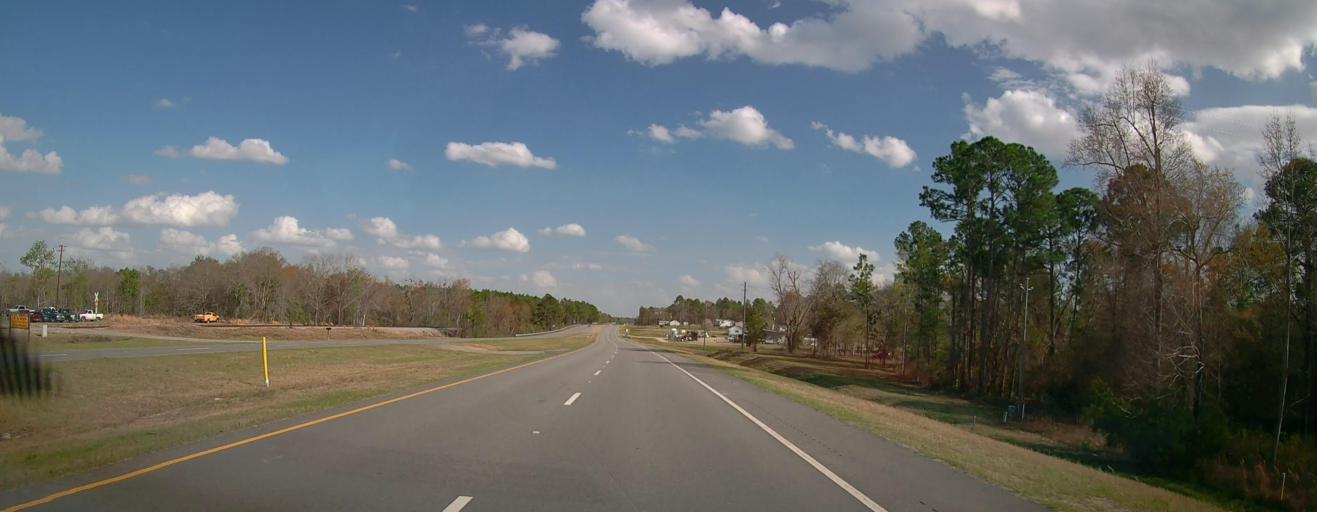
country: US
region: Georgia
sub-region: Telfair County
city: Helena
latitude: 32.0843
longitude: -82.9302
